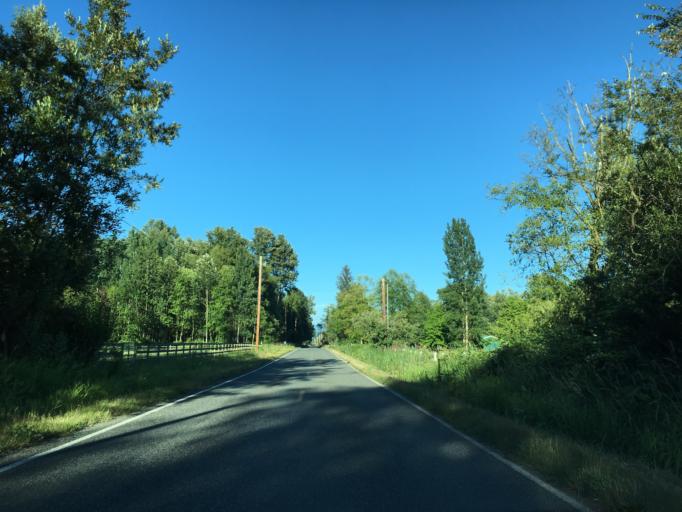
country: US
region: Washington
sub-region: Whatcom County
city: Ferndale
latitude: 48.9062
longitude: -122.5946
